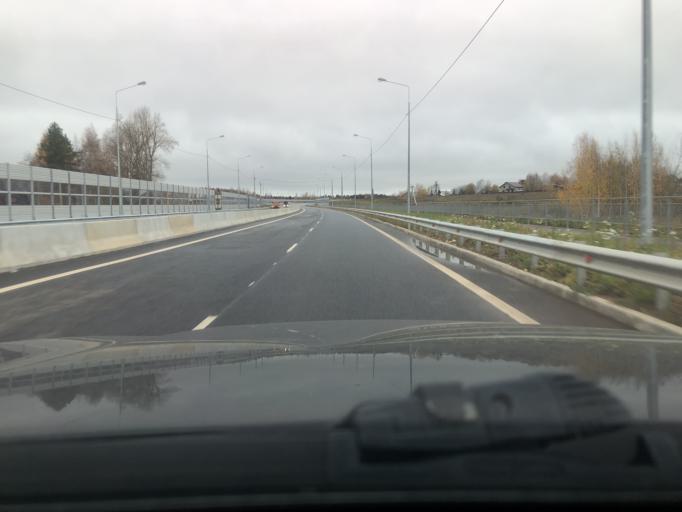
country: RU
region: Moskovskaya
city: Semkhoz
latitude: 56.3183
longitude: 38.0854
